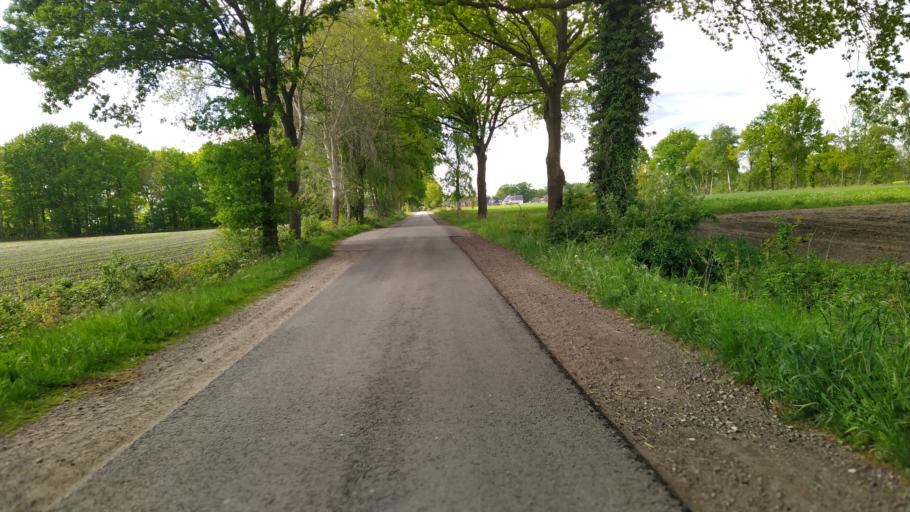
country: DE
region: Lower Saxony
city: Brest
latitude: 53.4453
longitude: 9.3939
